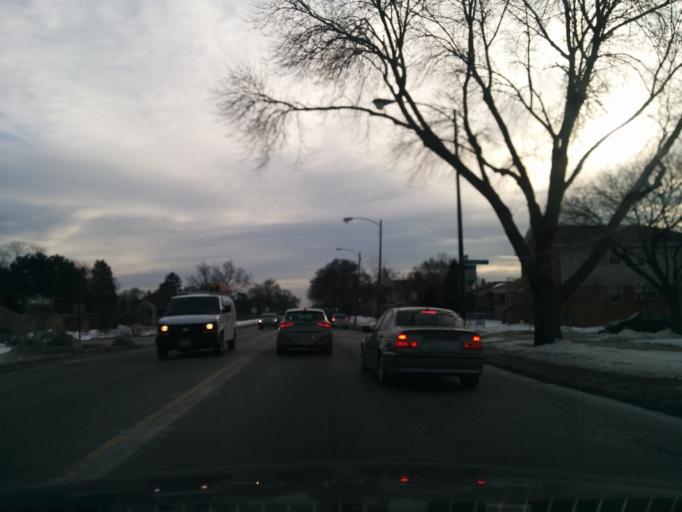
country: US
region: Illinois
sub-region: Cook County
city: Norridge
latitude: 41.9522
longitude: -87.8299
